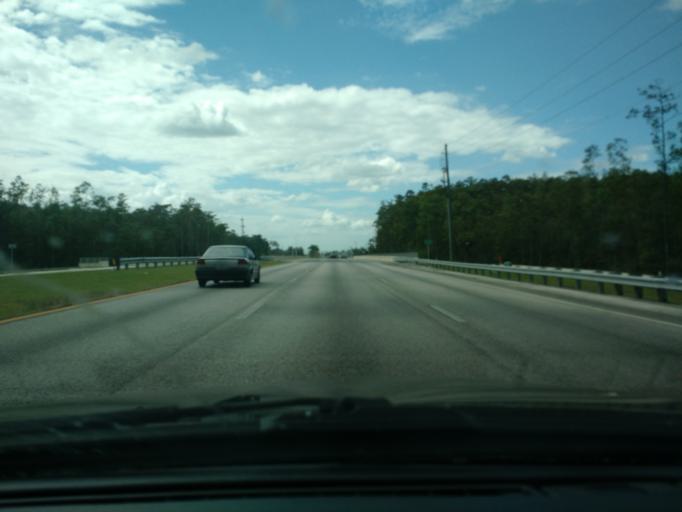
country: US
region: Florida
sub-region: Lee County
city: Fort Myers
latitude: 26.6131
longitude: -81.7898
